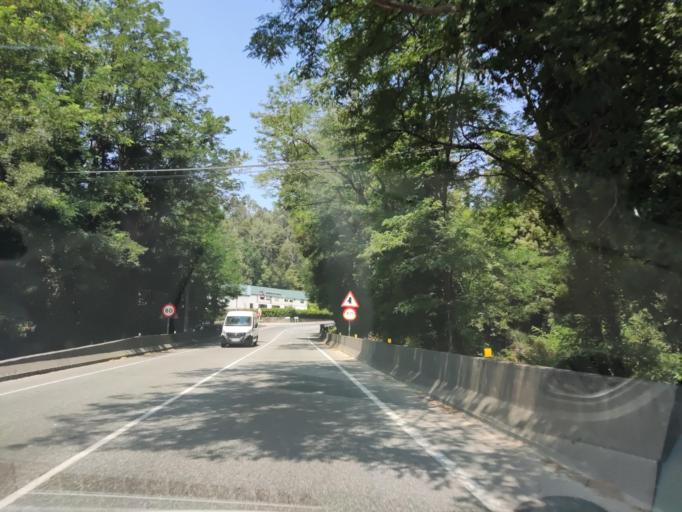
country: ES
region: Galicia
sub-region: Provincia de Pontevedra
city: Redondela
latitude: 42.2393
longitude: -8.5955
